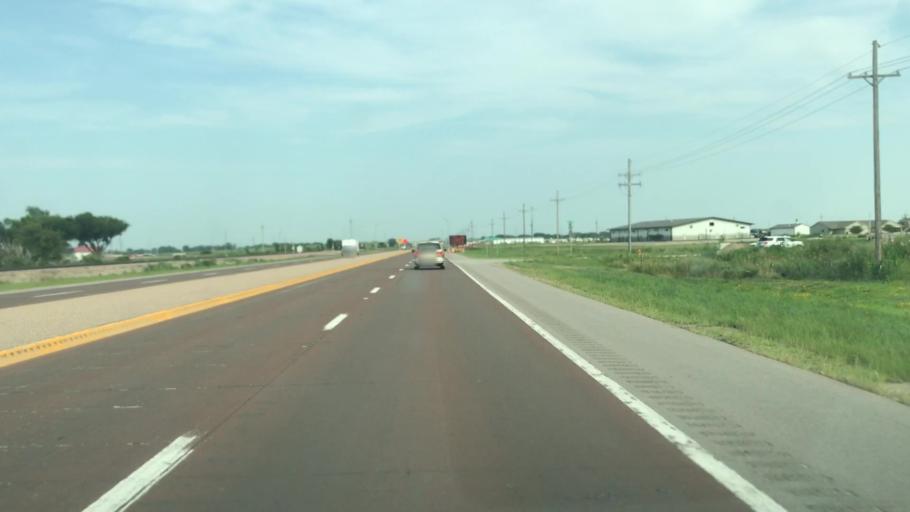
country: US
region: Nebraska
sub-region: Hall County
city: Grand Island
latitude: 40.9572
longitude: -98.4020
